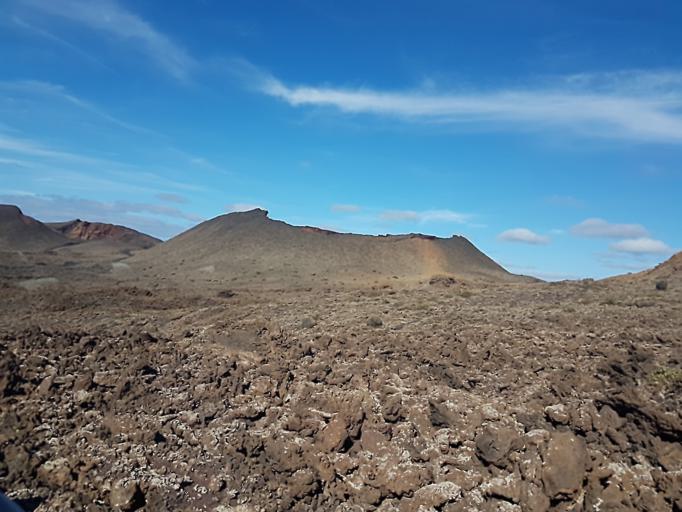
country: ES
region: Canary Islands
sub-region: Provincia de Las Palmas
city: Yaiza
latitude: 28.9956
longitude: -13.7551
